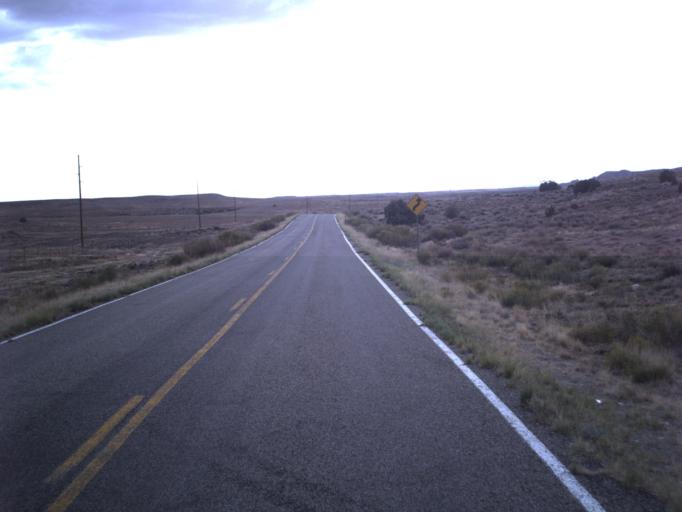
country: US
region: Utah
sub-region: San Juan County
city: Blanding
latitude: 37.4185
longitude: -109.4288
